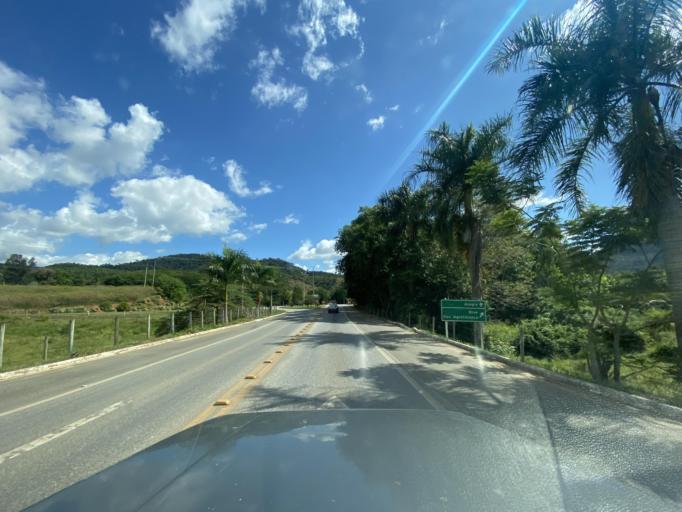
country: BR
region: Espirito Santo
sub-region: Jeronimo Monteiro
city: Jeronimo Monteiro
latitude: -20.7615
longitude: -41.4557
